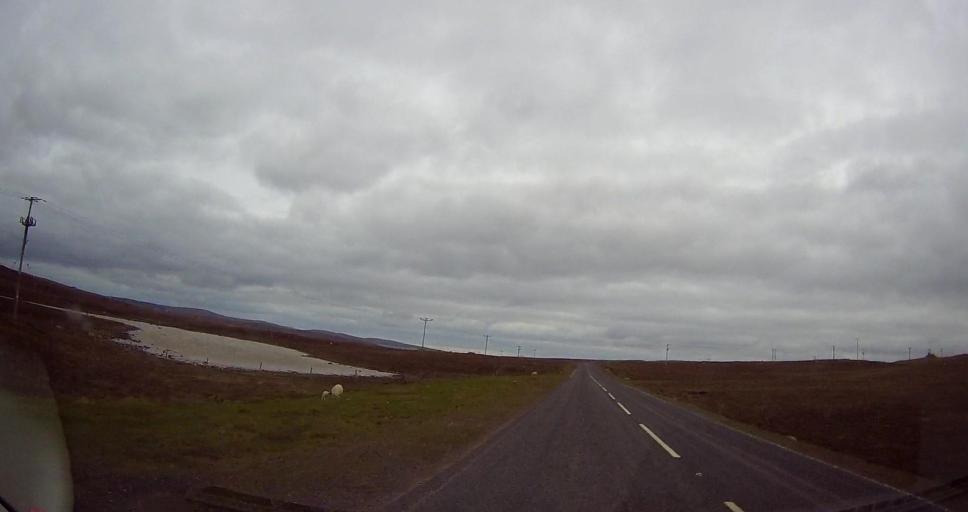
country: GB
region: Scotland
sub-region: Shetland Islands
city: Shetland
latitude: 60.7133
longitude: -0.9159
